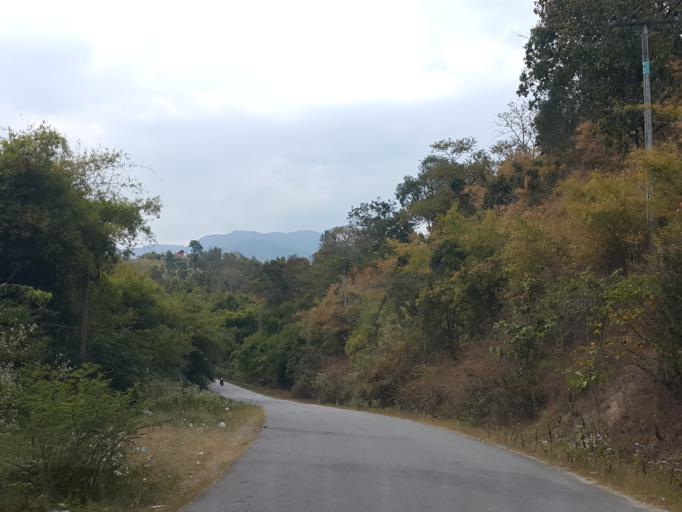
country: TH
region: Chiang Mai
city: Om Koi
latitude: 17.7984
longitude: 98.3448
